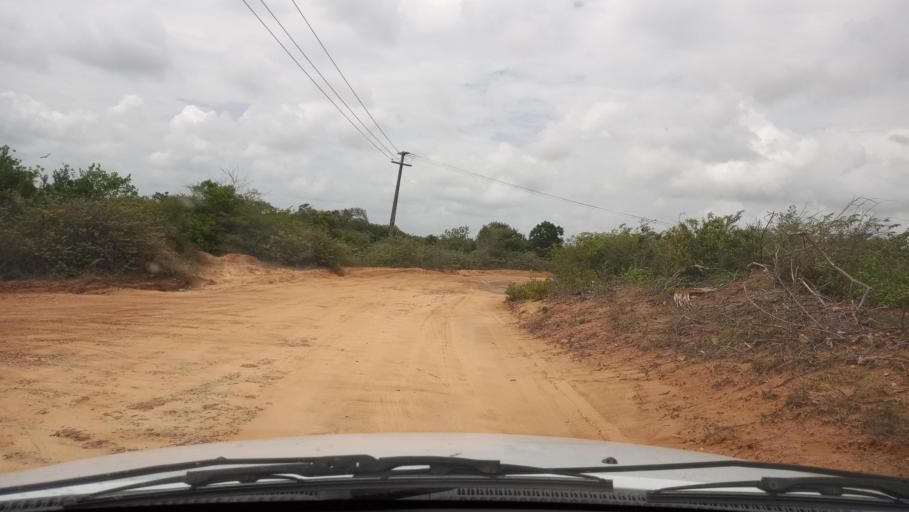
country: BR
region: Rio Grande do Norte
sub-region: Maxaranguape
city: Sao Miguel
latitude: -5.4824
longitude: -35.3037
